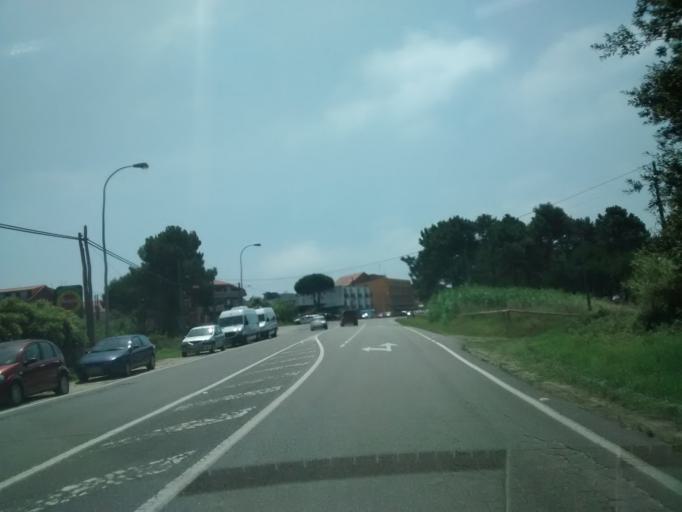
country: ES
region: Galicia
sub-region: Provincia de Pontevedra
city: Sanxenxo
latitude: 42.3992
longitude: -8.8462
